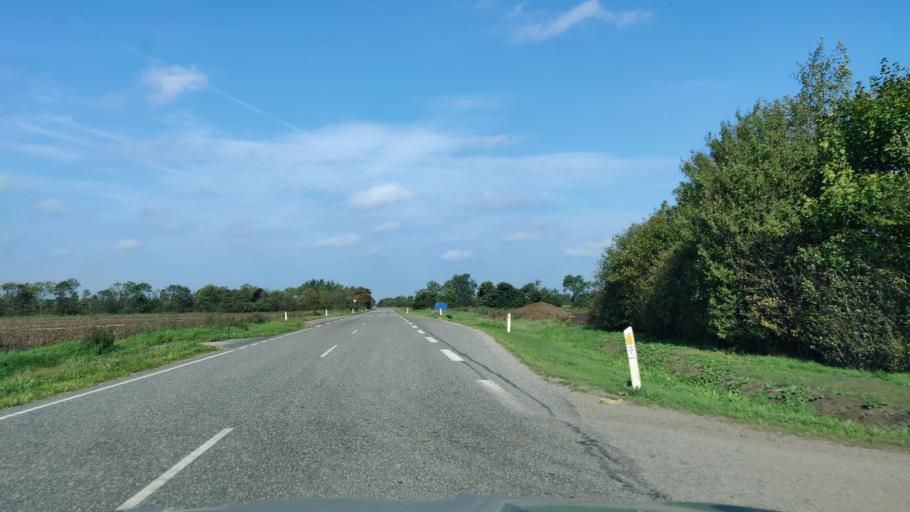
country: DK
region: Central Jutland
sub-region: Herning Kommune
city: Sunds
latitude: 56.2532
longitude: 9.0512
